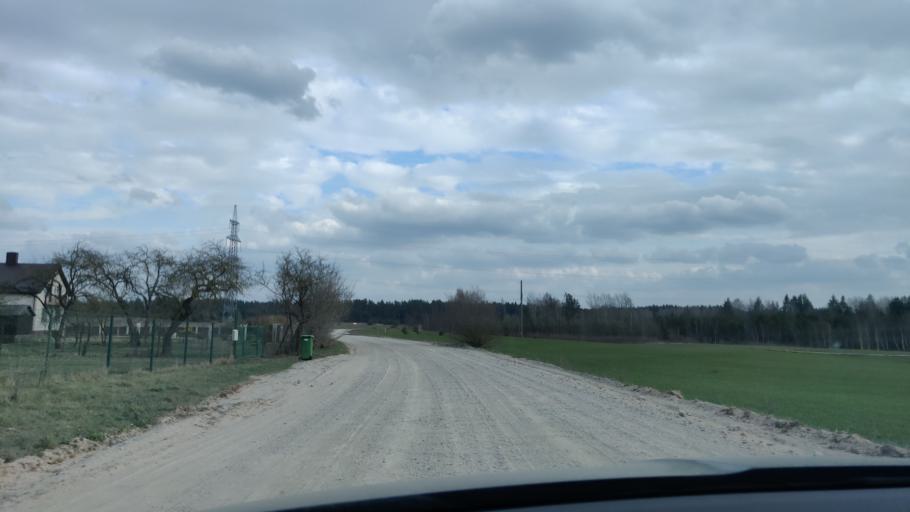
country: LT
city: Lentvaris
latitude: 54.6097
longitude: 25.0714
